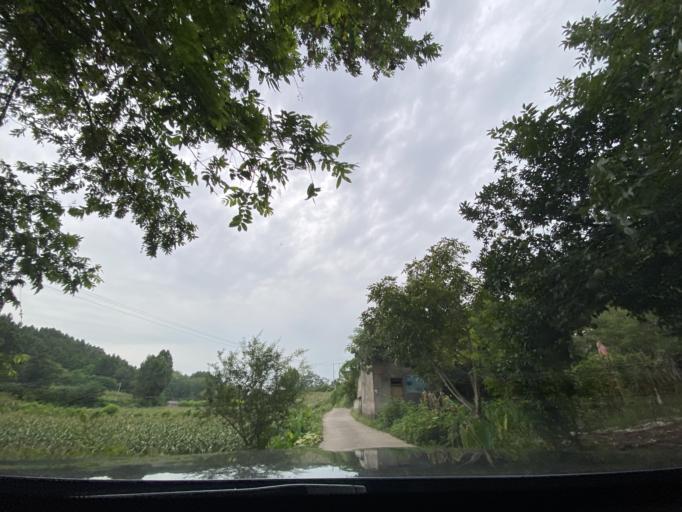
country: CN
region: Sichuan
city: Jiancheng
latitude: 30.3861
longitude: 104.4846
